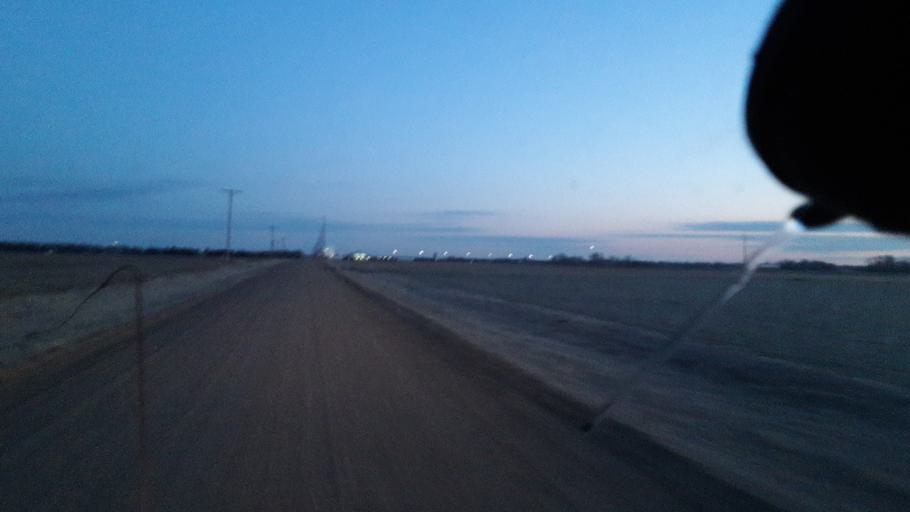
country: US
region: Kansas
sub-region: Reno County
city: South Hutchinson
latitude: 38.0089
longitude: -97.9768
